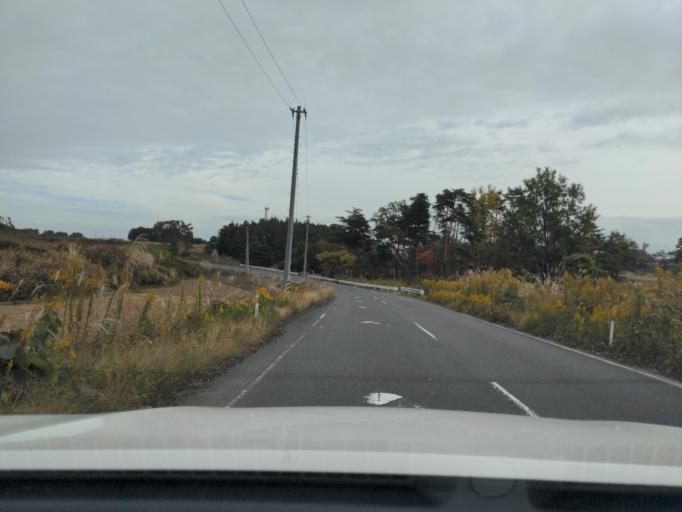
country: JP
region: Fukushima
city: Koriyama
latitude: 37.3647
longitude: 140.2905
